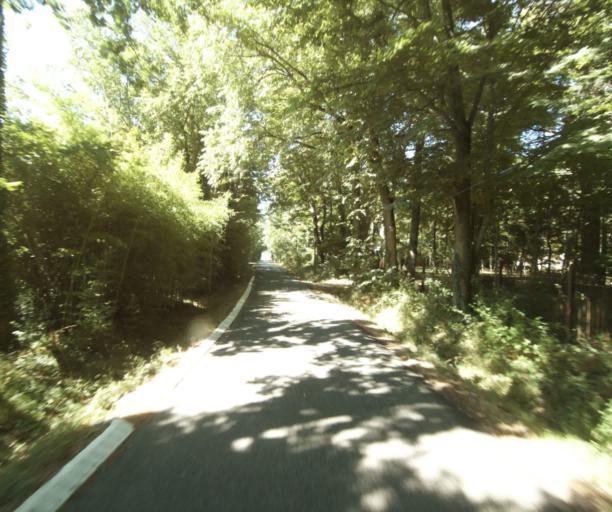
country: FR
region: Midi-Pyrenees
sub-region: Departement de la Haute-Garonne
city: Saint-Felix-Lauragais
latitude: 43.5106
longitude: 1.8899
